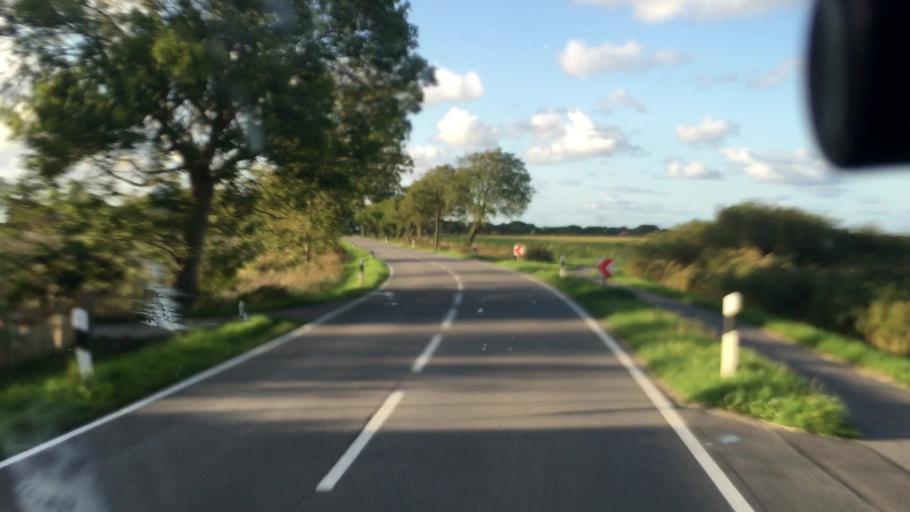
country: DE
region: Lower Saxony
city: Neuharlingersiel
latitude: 53.6850
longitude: 7.6871
